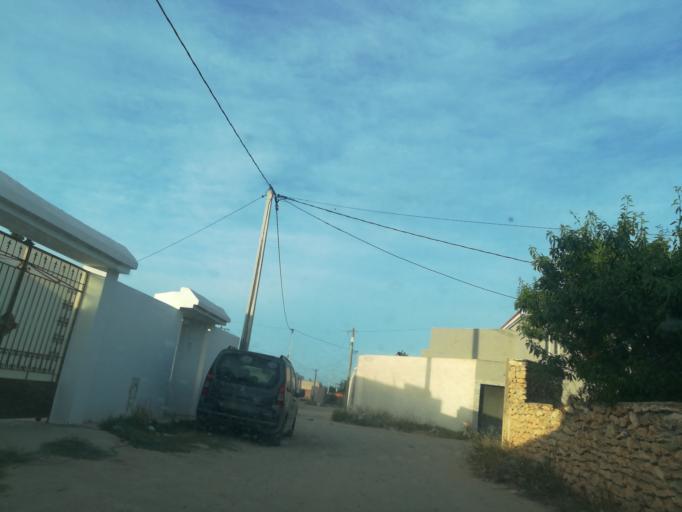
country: TN
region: Safaqis
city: Al Qarmadah
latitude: 34.8207
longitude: 10.7589
